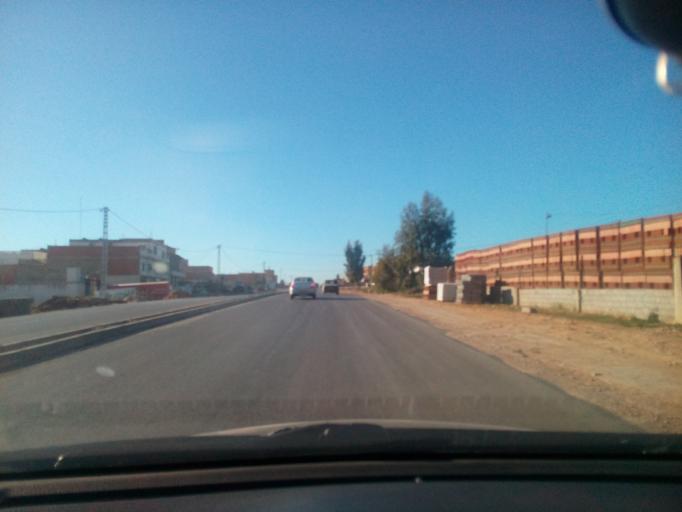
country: DZ
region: Mostaganem
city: Mostaganem
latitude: 35.9093
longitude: 0.1637
